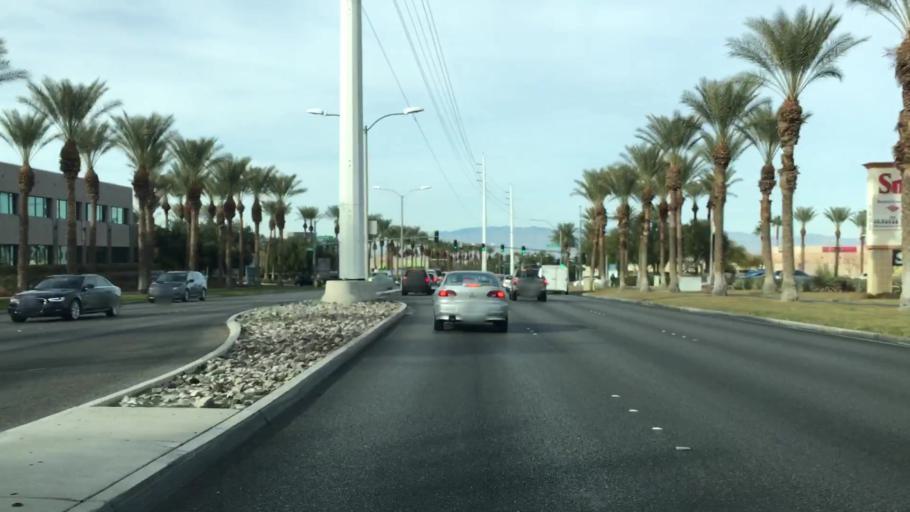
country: US
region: Nevada
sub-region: Clark County
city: Whitney
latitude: 36.0270
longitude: -115.0857
